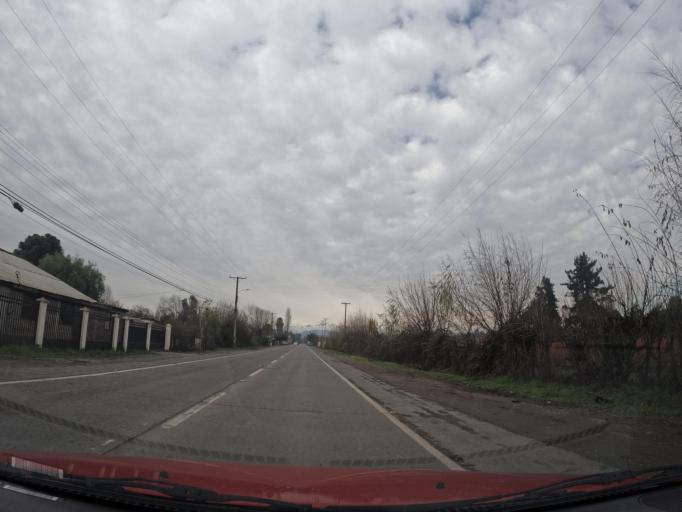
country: CL
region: Maule
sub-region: Provincia de Linares
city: Linares
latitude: -35.8593
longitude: -71.5753
